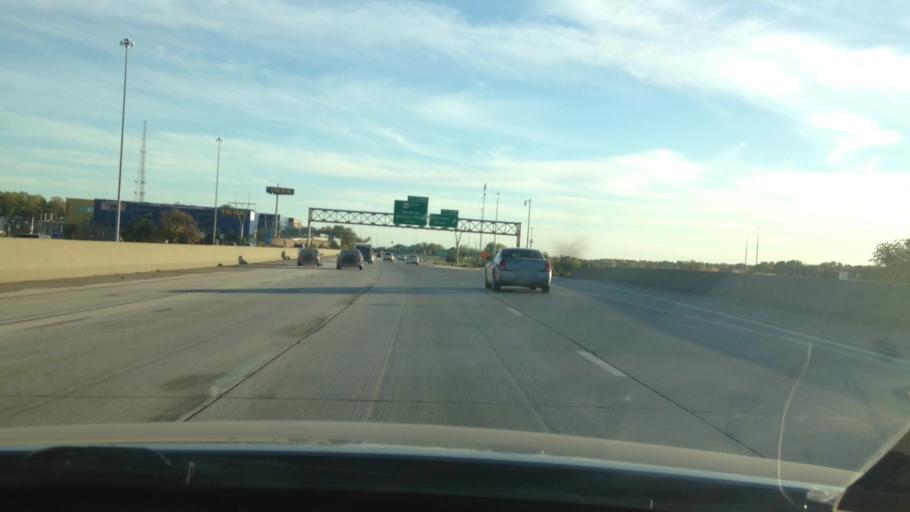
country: US
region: Kansas
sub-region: Johnson County
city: Merriam
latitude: 39.0258
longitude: -94.6912
